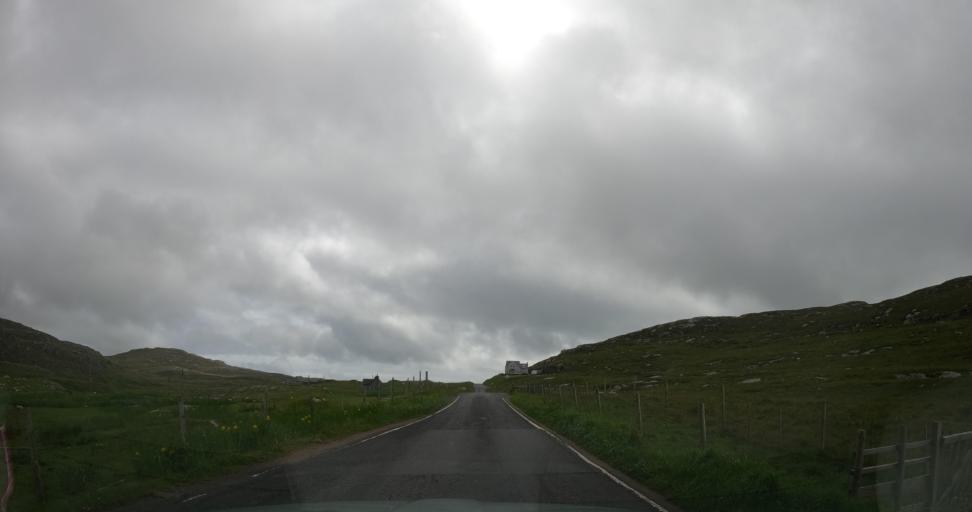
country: GB
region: Scotland
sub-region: Eilean Siar
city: Barra
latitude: 56.9641
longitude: -7.5103
